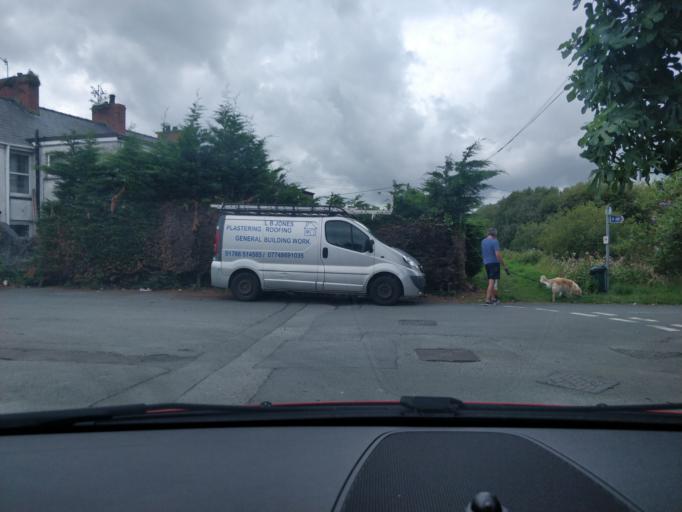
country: GB
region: Wales
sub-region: Gwynedd
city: Porthmadog
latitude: 52.9293
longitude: -4.1296
